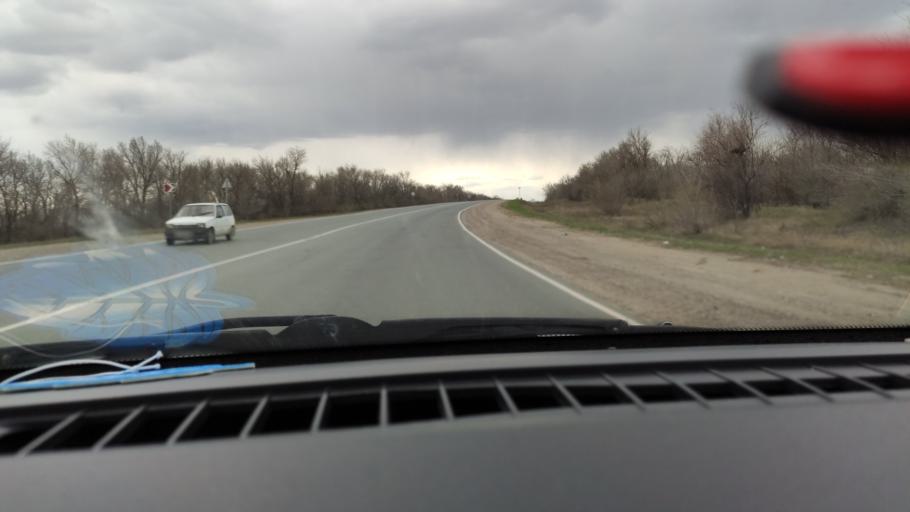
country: RU
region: Saratov
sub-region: Saratovskiy Rayon
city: Saratov
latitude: 51.7119
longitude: 46.0207
